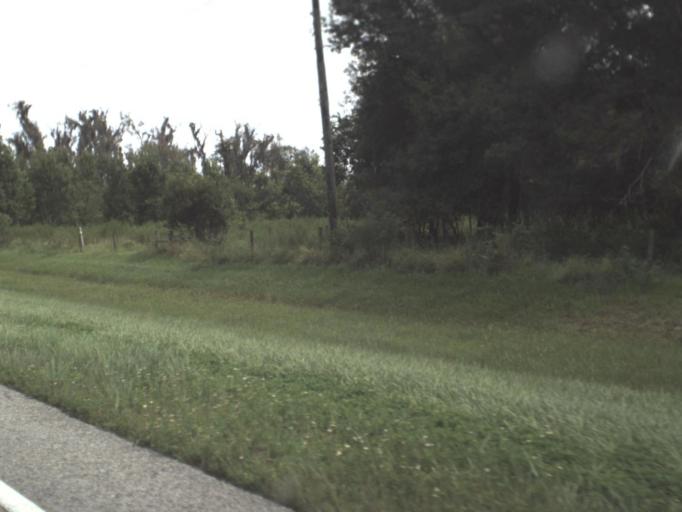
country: US
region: Florida
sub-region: DeSoto County
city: Arcadia
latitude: 27.3107
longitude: -81.8182
